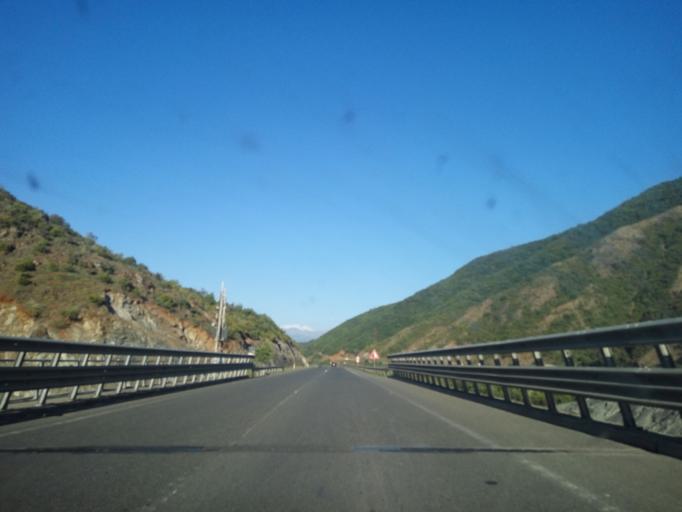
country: AL
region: Lezhe
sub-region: Rrethi i Mirdites
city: Rreshen
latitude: 41.7811
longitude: 19.8350
